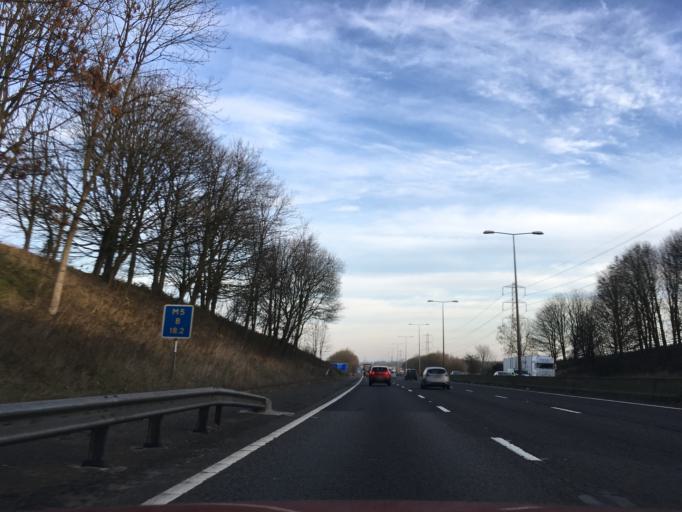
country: GB
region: England
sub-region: City and Borough of Birmingham
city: Bartley Green
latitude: 52.4128
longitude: -2.0267
